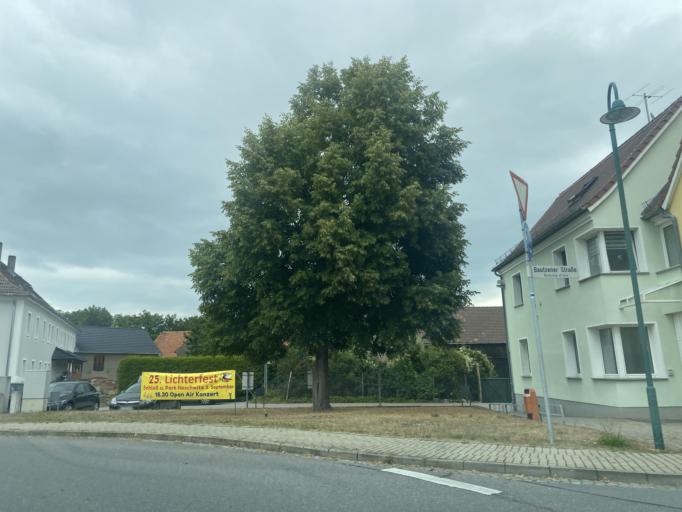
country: DE
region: Saxony
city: Neschwitz
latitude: 51.2707
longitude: 14.3292
